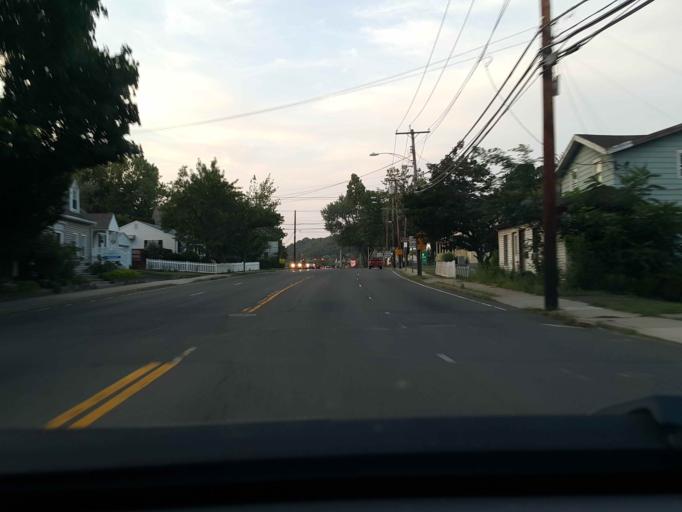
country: US
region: Connecticut
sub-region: New Haven County
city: East Haven
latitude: 41.2742
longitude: -72.8694
